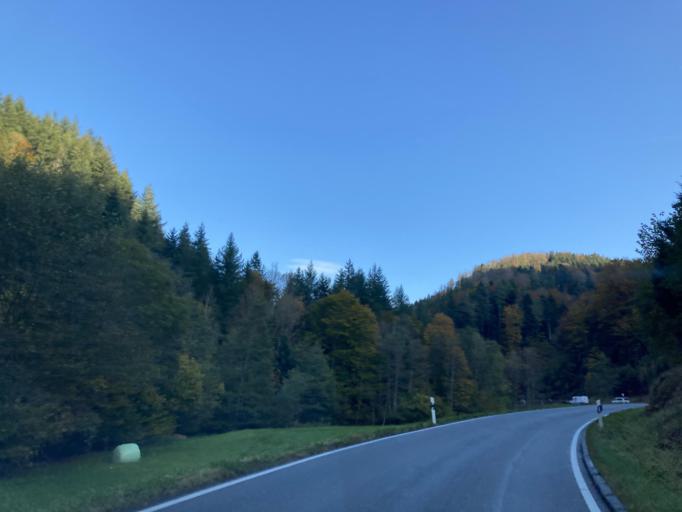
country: DE
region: Baden-Wuerttemberg
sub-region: Freiburg Region
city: Buchenbach
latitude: 47.9712
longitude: 8.0564
